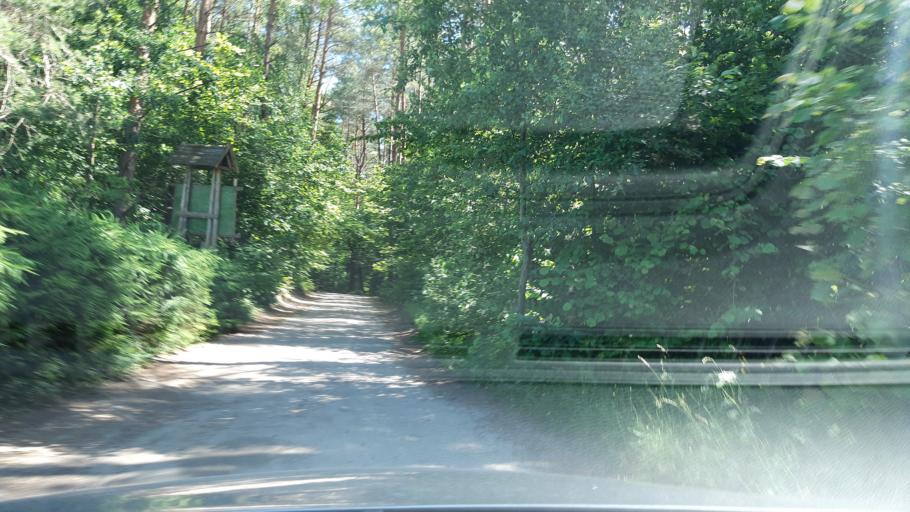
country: PL
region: Warmian-Masurian Voivodeship
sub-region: Powiat piski
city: Ruciane-Nida
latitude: 53.7125
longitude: 21.4904
